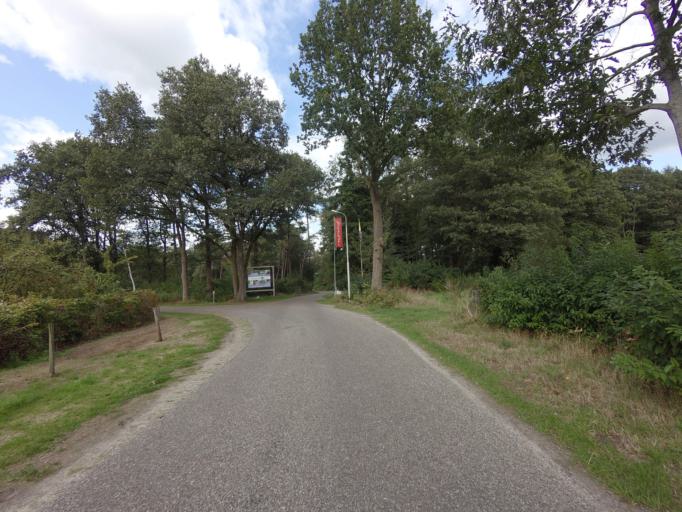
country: NL
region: Drenthe
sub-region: Gemeente De Wolden
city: Ruinen
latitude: 52.7809
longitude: 6.3669
